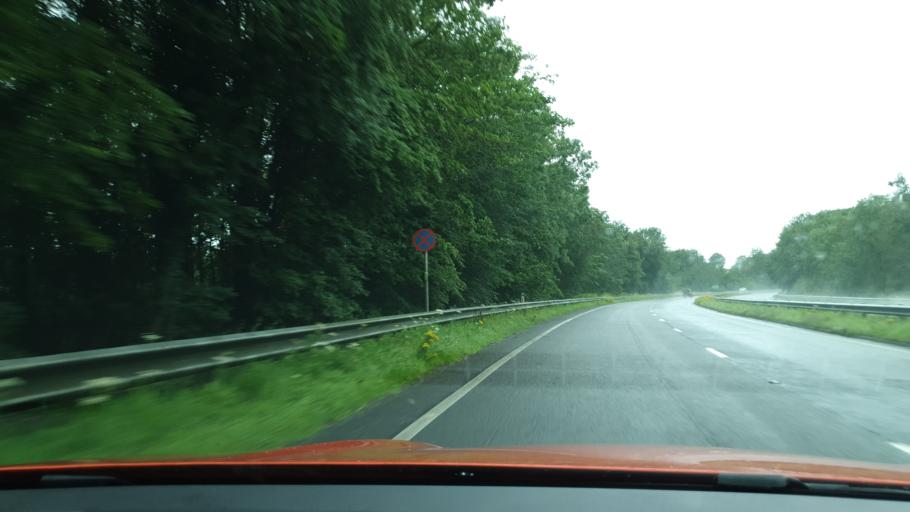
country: GB
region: England
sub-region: Cumbria
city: Grange-over-Sands
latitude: 54.2186
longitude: -2.8962
